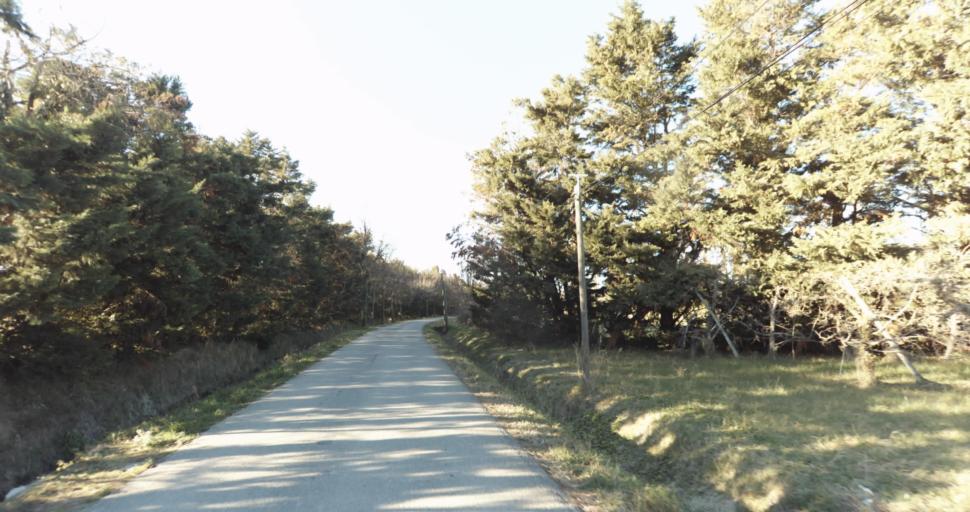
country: FR
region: Provence-Alpes-Cote d'Azur
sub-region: Departement des Bouches-du-Rhone
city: Barbentane
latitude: 43.9031
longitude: 4.7523
